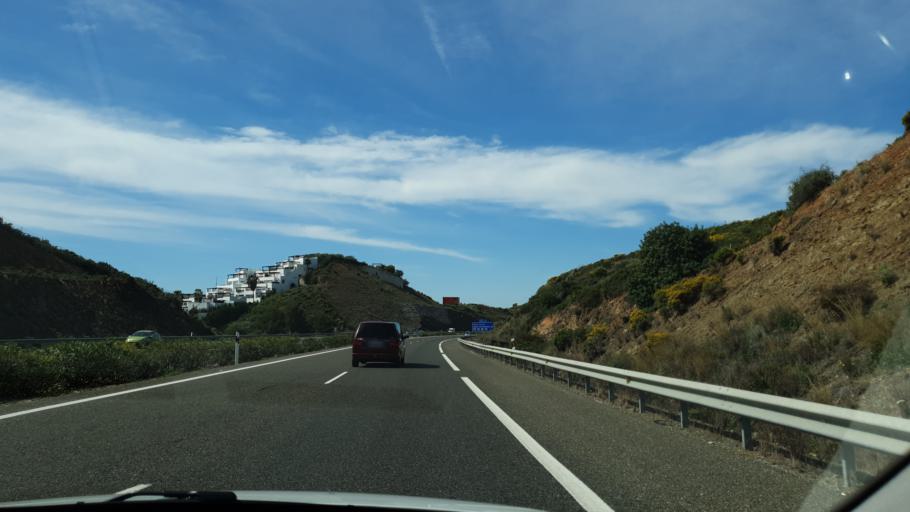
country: ES
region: Andalusia
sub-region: Provincia de Malaga
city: Ojen
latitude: 36.5157
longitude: -4.8161
